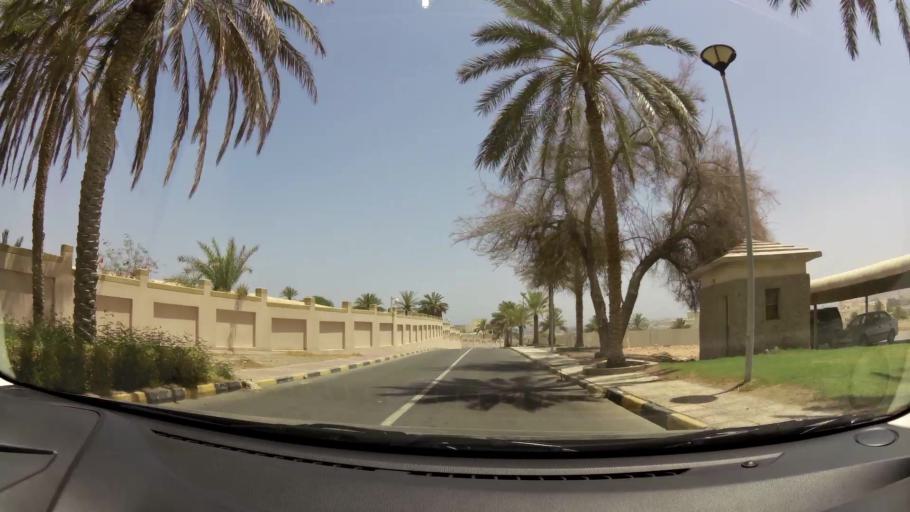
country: OM
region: Muhafazat Masqat
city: Bawshar
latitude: 23.6022
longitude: 58.4695
